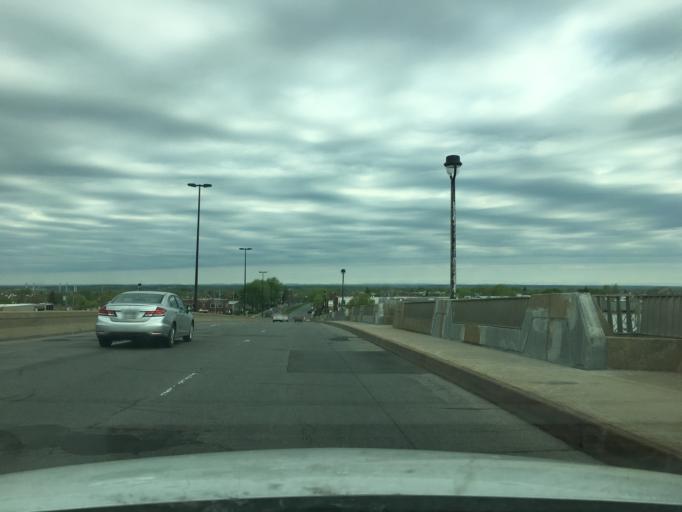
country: CA
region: Quebec
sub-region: Montreal
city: Saint-Leonard
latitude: 45.6275
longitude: -73.5844
